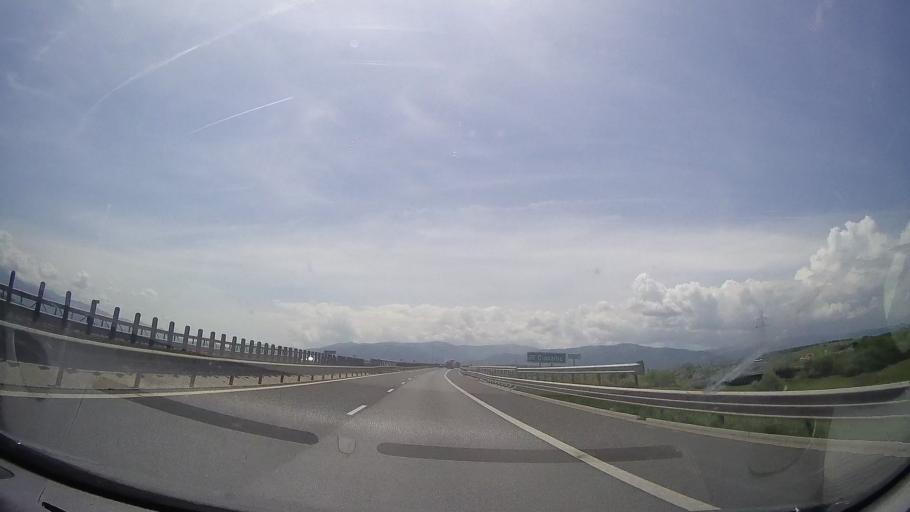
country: RO
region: Sibiu
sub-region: Comuna Selimbar
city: Selimbar
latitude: 45.7569
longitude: 24.2063
